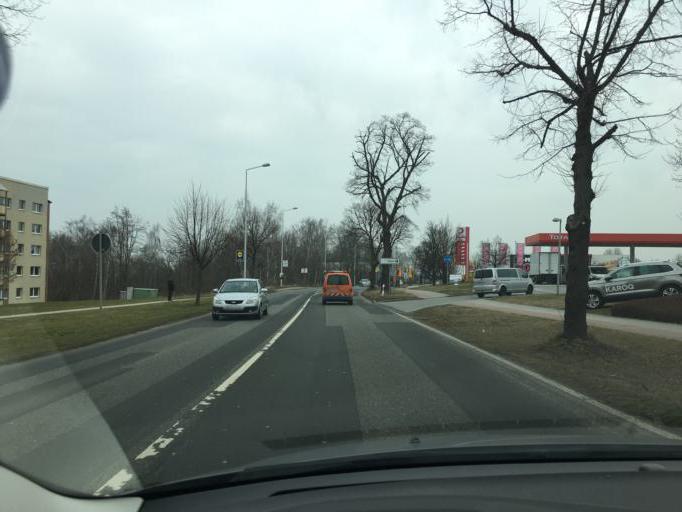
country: DE
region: Thuringia
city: Altenburg
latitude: 51.0075
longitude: 12.4528
